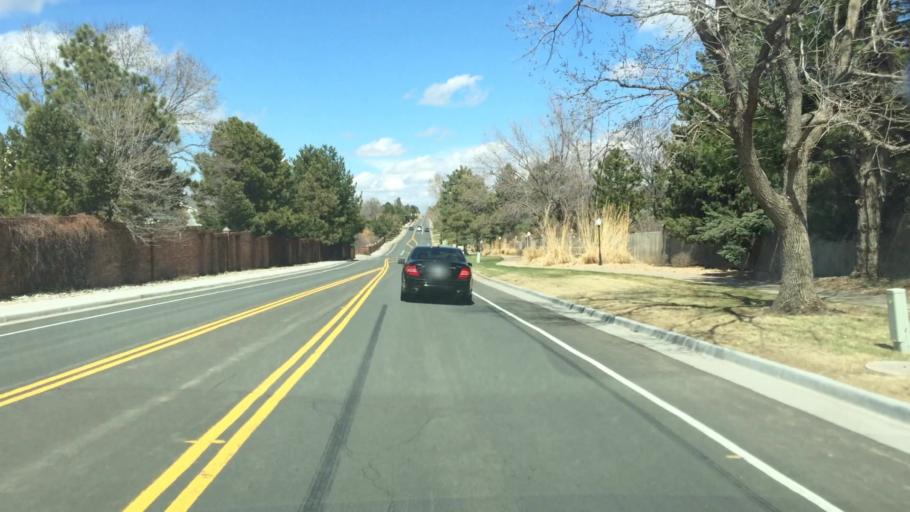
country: US
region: Colorado
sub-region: Arapahoe County
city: Centennial
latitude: 39.6061
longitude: -104.8761
